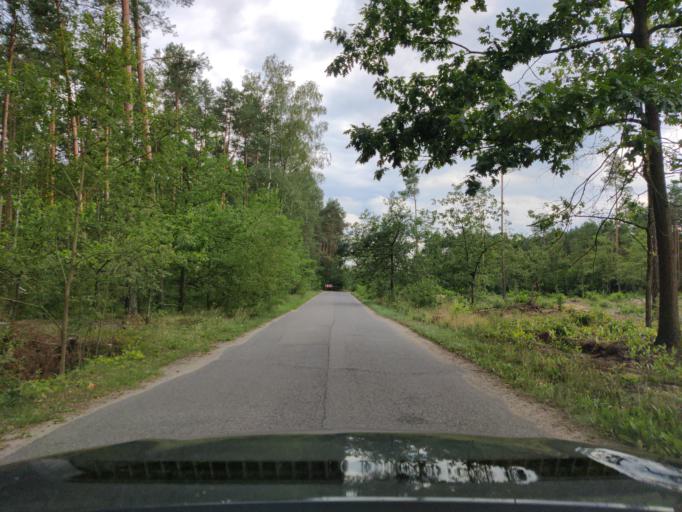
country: PL
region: Masovian Voivodeship
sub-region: Powiat pultuski
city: Pultusk
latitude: 52.7302
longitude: 21.1375
